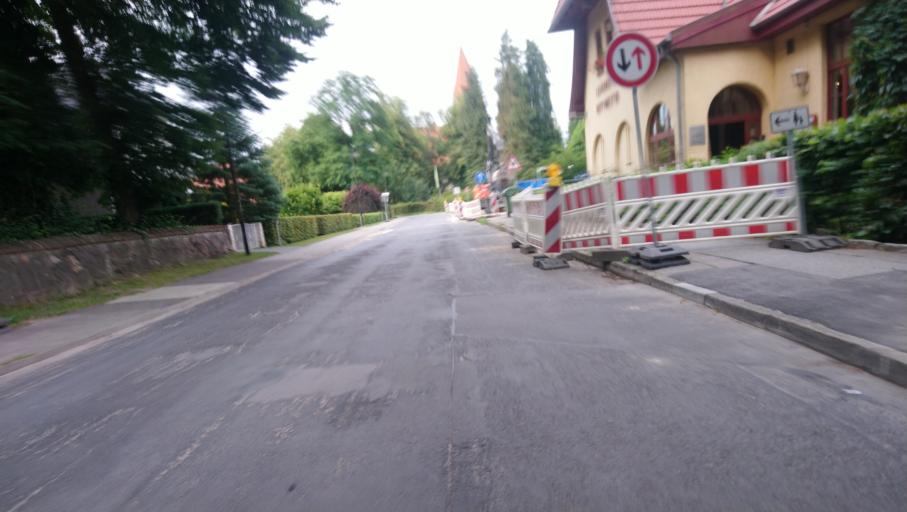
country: DE
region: Mecklenburg-Vorpommern
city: Papendorf
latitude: 54.0630
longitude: 12.1043
